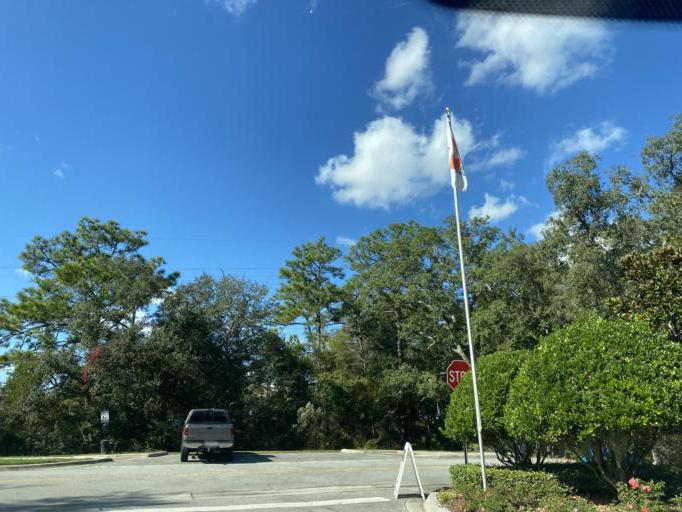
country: US
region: Florida
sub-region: Seminole County
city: Heathrow
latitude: 28.7883
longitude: -81.3449
